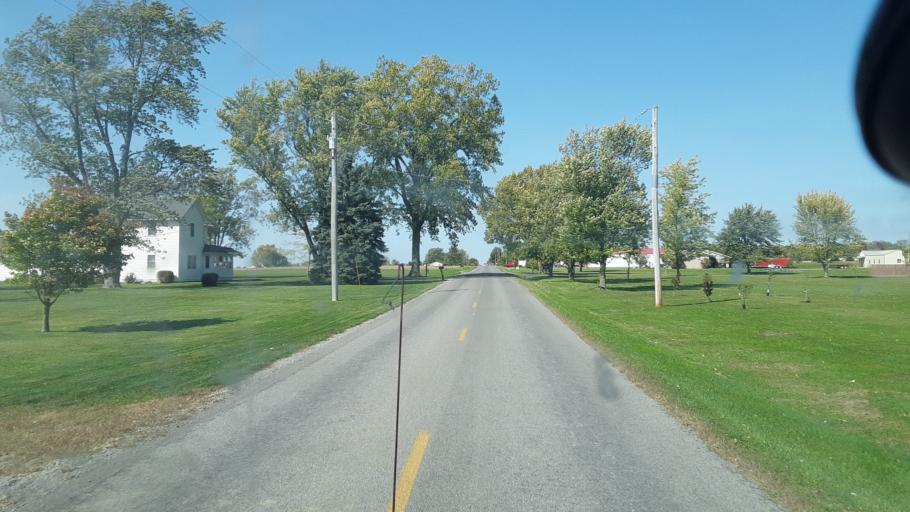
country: US
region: Ohio
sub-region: Logan County
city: Northwood
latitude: 40.5044
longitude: -83.7862
